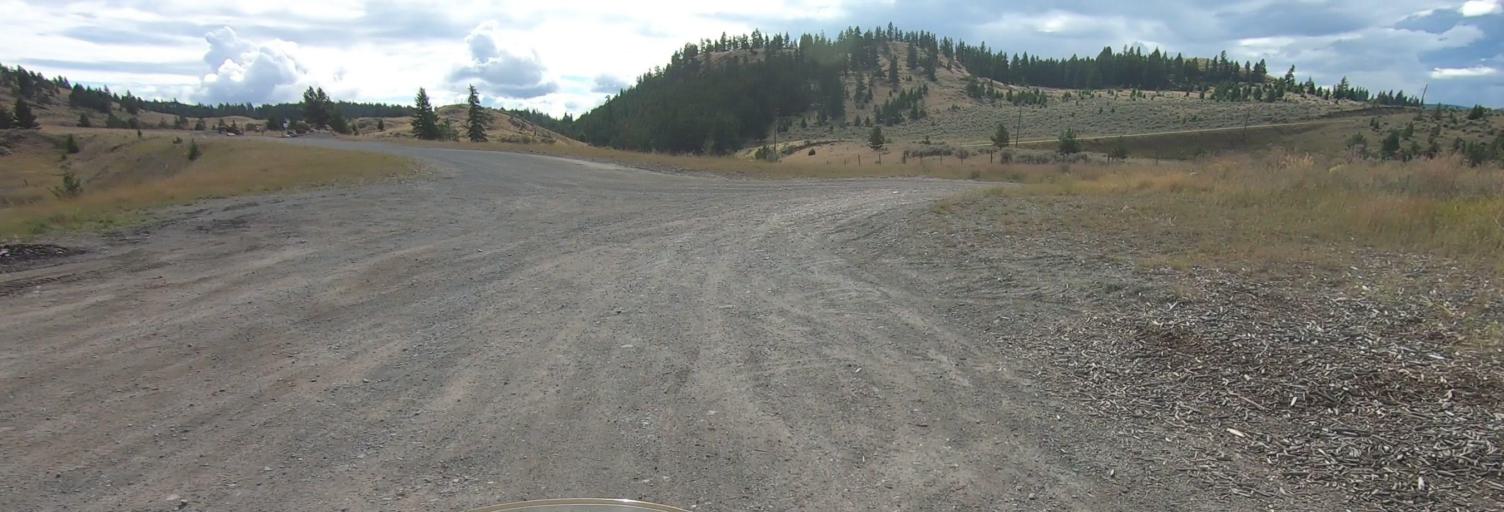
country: CA
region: British Columbia
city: Kamloops
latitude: 50.6156
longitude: -120.4446
